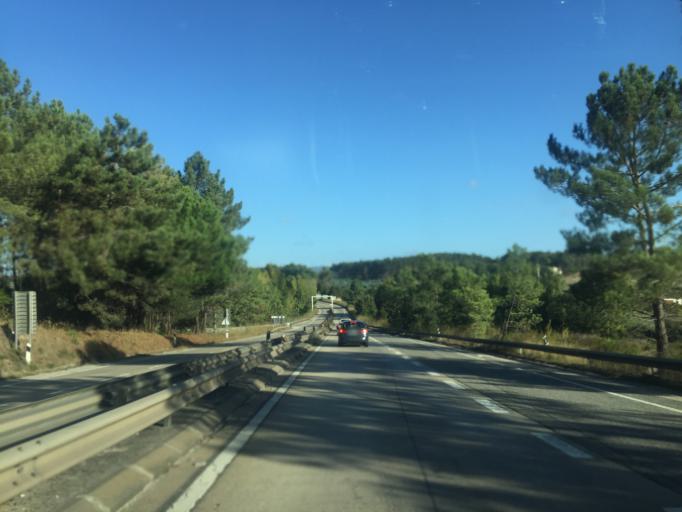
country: PT
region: Santarem
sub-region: Rio Maior
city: Rio Maior
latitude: 39.3129
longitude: -8.9363
